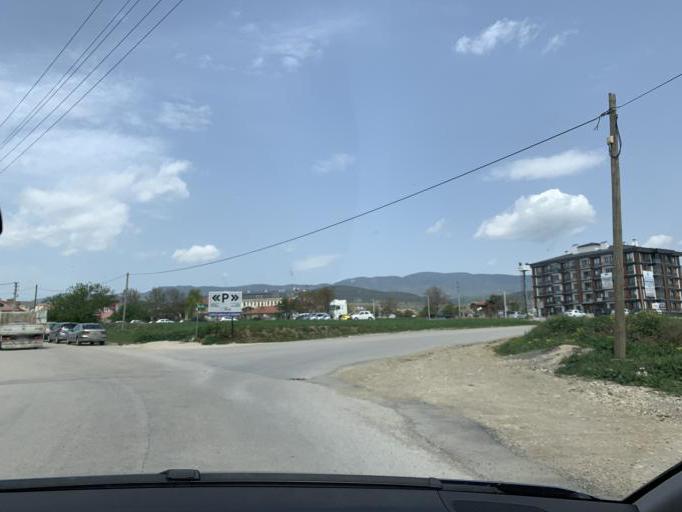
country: TR
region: Bolu
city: Bolu
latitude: 40.7326
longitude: 31.5651
